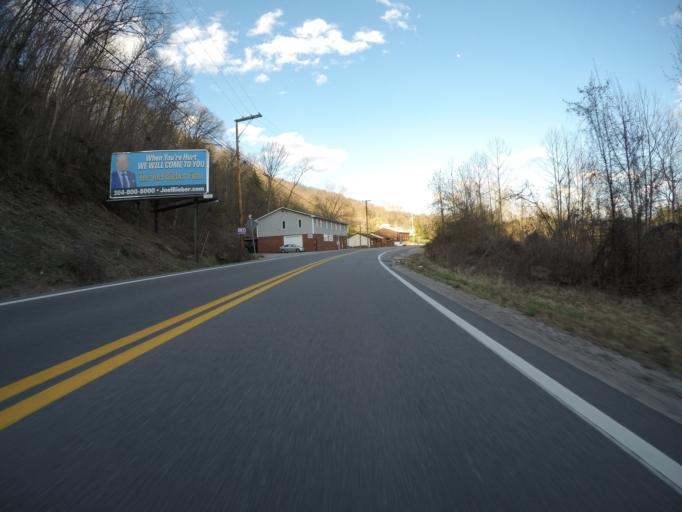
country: US
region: West Virginia
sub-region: Kanawha County
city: Charleston
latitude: 38.4002
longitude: -81.5821
